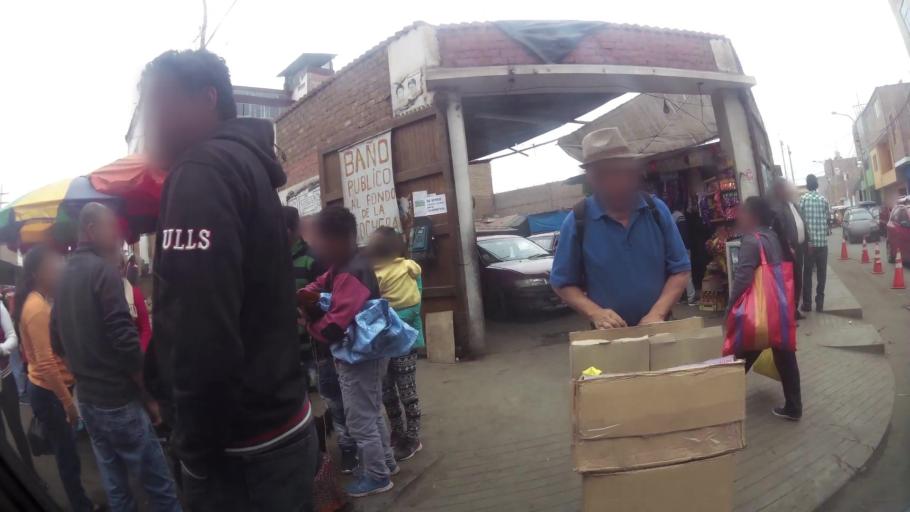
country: PE
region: Lima
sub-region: Provincia de Huaral
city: Chancay
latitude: -11.5649
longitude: -77.2705
